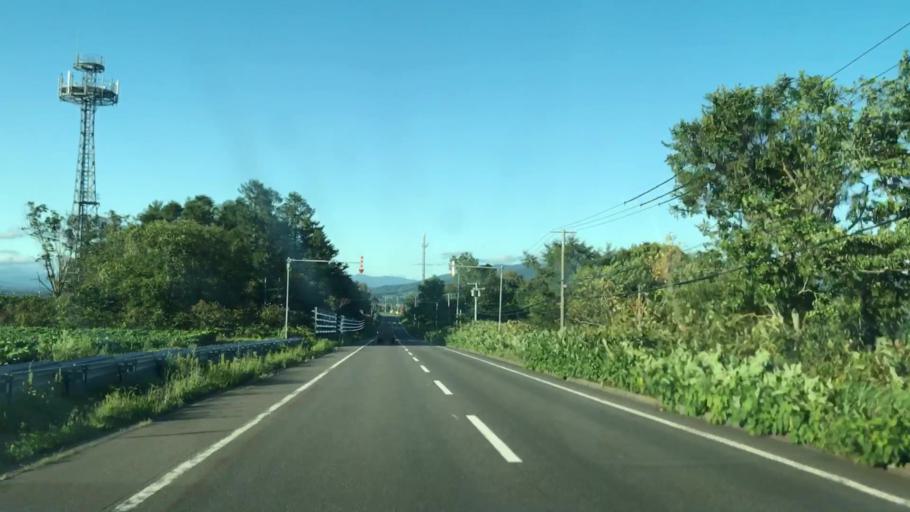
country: JP
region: Hokkaido
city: Date
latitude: 42.6225
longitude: 140.7953
